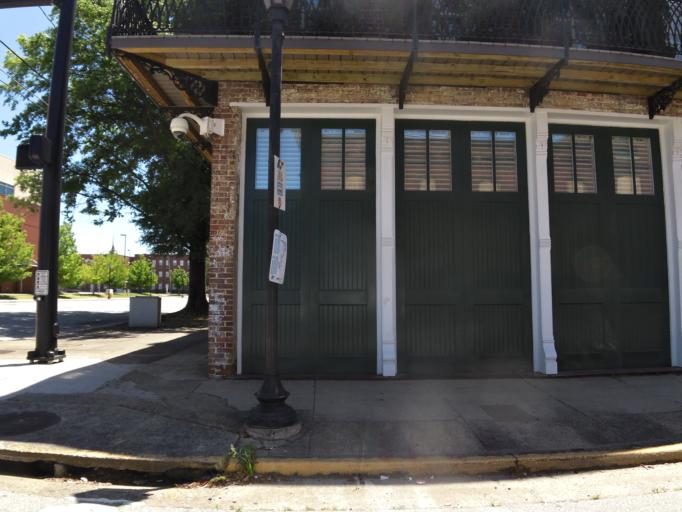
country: US
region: Georgia
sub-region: Richmond County
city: Augusta
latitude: 33.4727
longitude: -81.9691
